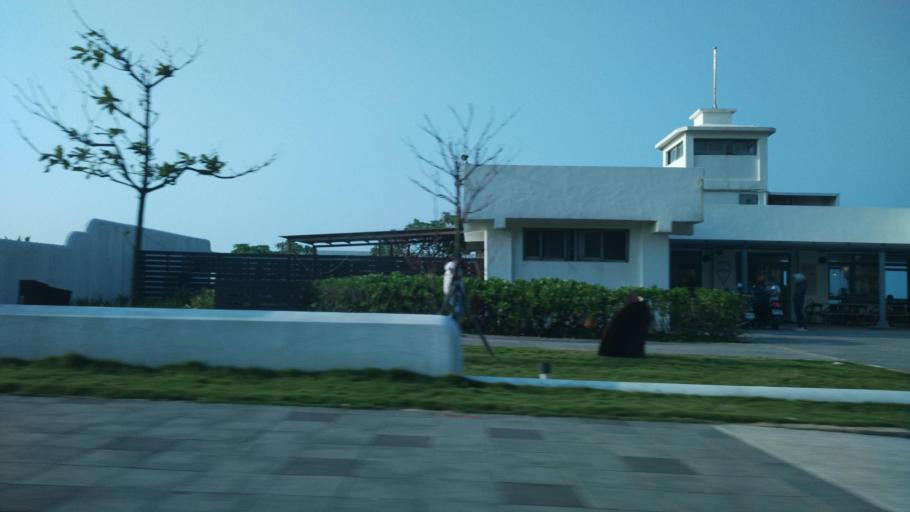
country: TW
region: Taipei
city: Taipei
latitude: 25.2856
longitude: 121.5234
